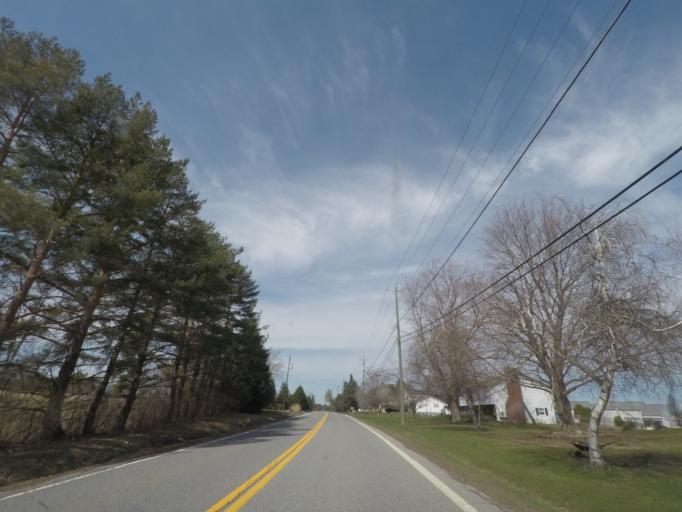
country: US
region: New York
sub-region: Saratoga County
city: Mechanicville
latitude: 42.9037
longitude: -73.7167
